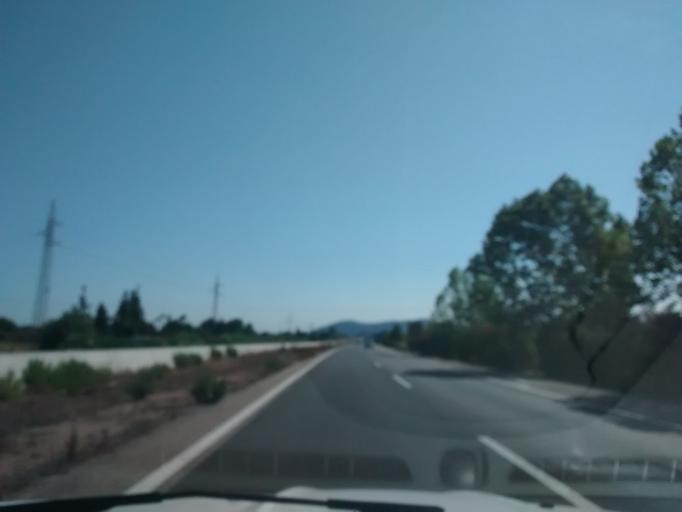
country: ES
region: Balearic Islands
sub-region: Illes Balears
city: Lloseta
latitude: 39.6997
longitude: 2.8872
